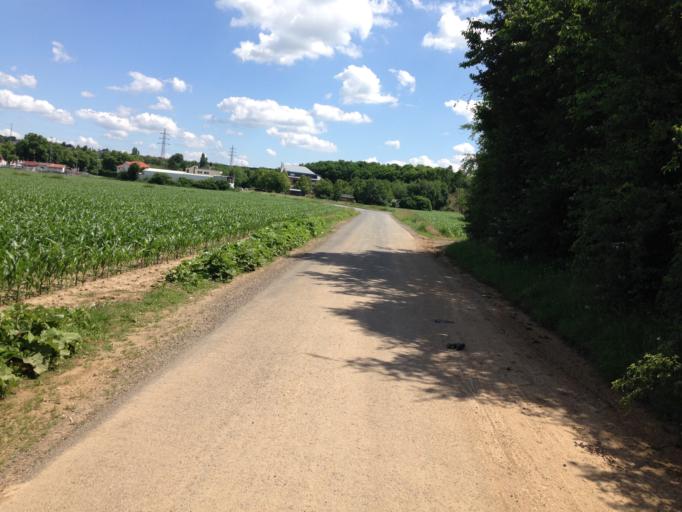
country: DE
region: Hesse
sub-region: Regierungsbezirk Giessen
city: Heuchelheim
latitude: 50.5703
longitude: 8.6444
